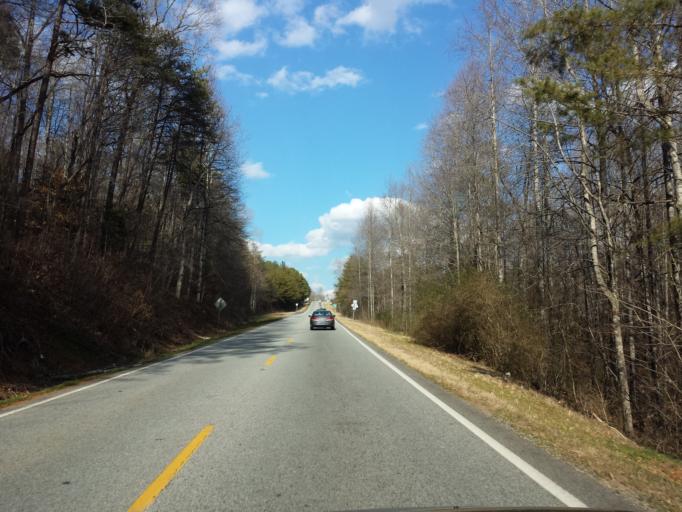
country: US
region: Georgia
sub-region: Lumpkin County
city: Dahlonega
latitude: 34.5183
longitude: -83.9188
